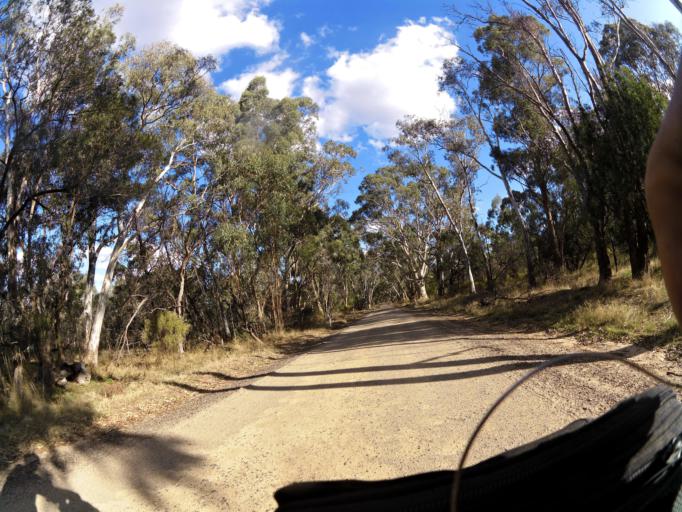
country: AU
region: Victoria
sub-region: Greater Bendigo
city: Kennington
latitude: -37.0088
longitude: 144.8098
